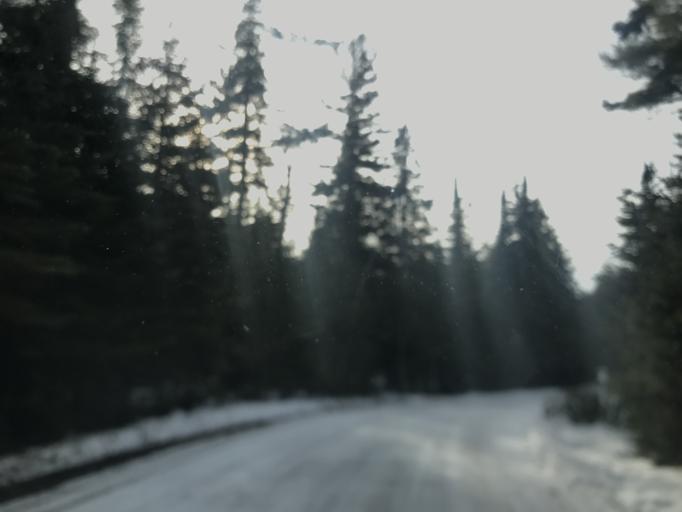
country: US
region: Wisconsin
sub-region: Door County
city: Sturgeon Bay
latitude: 45.1407
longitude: -87.0419
